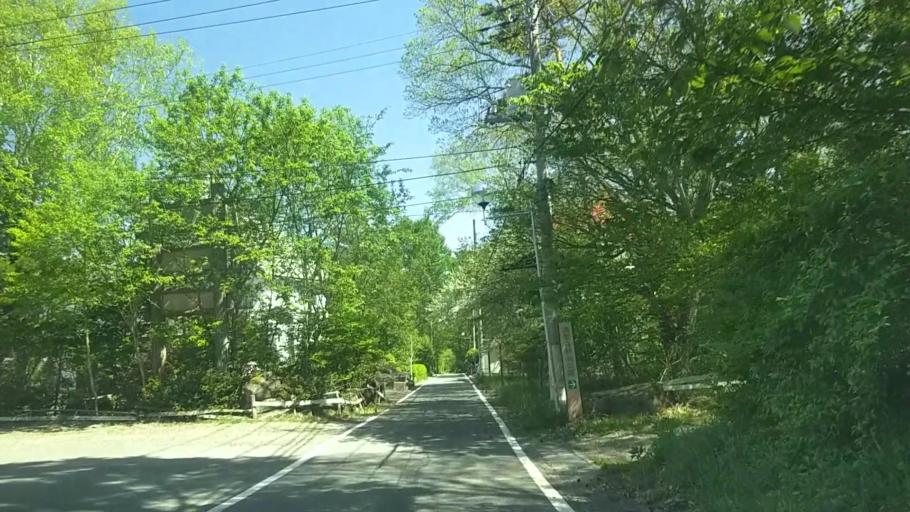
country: JP
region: Yamanashi
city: Nirasaki
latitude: 35.9172
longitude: 138.4376
